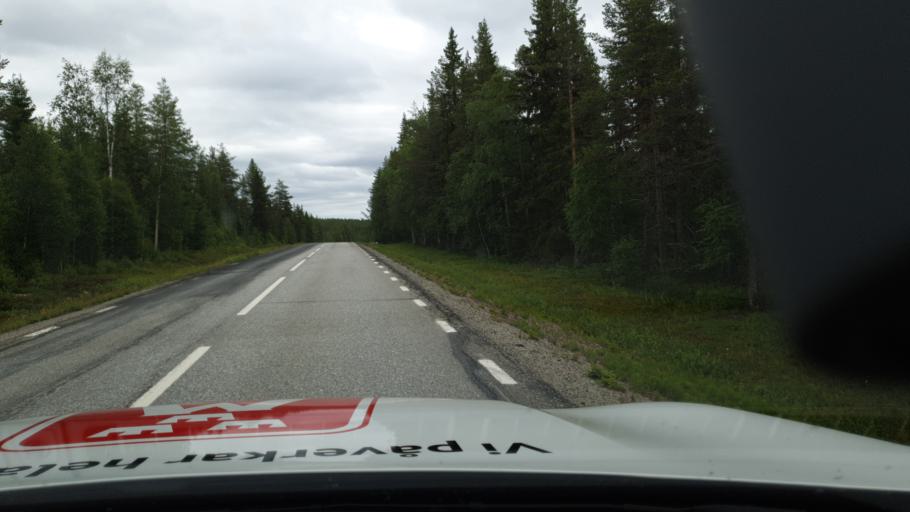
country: SE
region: Vaesterbotten
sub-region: Lycksele Kommun
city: Soderfors
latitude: 64.6913
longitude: 17.7719
